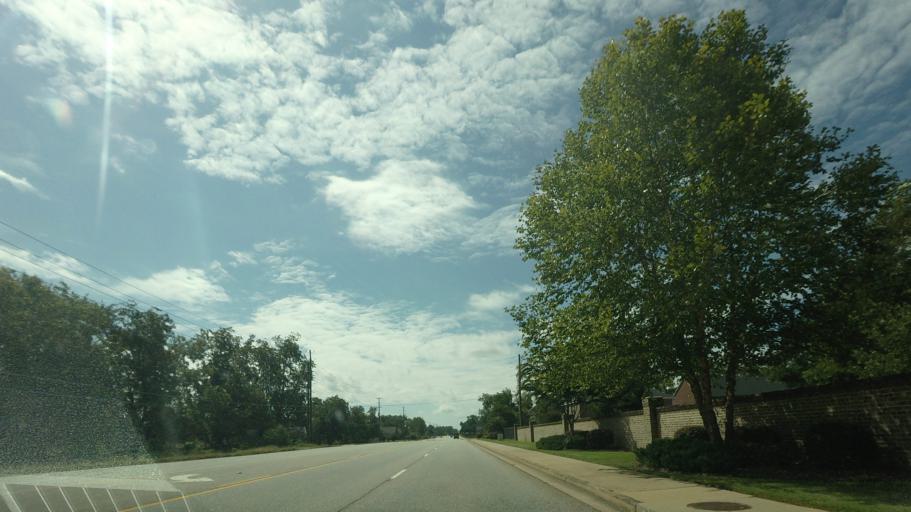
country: US
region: Georgia
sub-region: Houston County
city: Centerville
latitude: 32.5675
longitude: -83.6913
